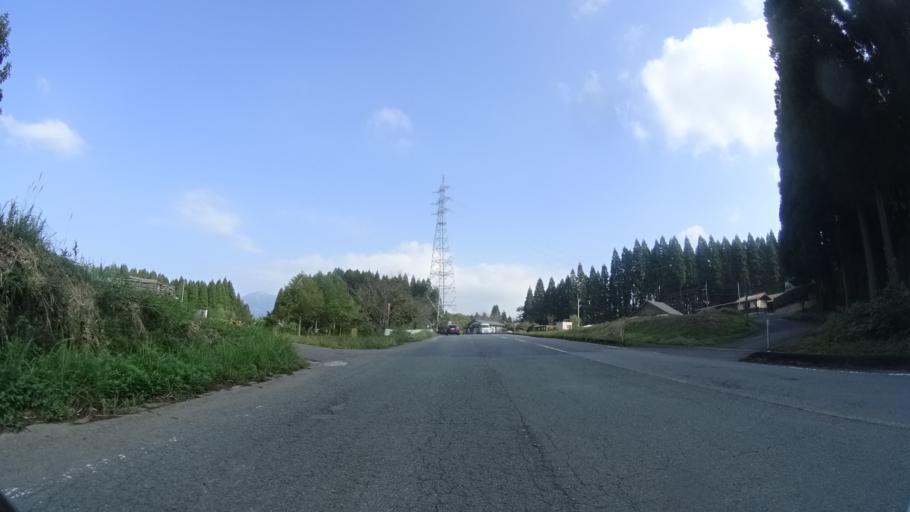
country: JP
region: Oita
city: Tsukawaki
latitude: 33.1260
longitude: 131.0758
